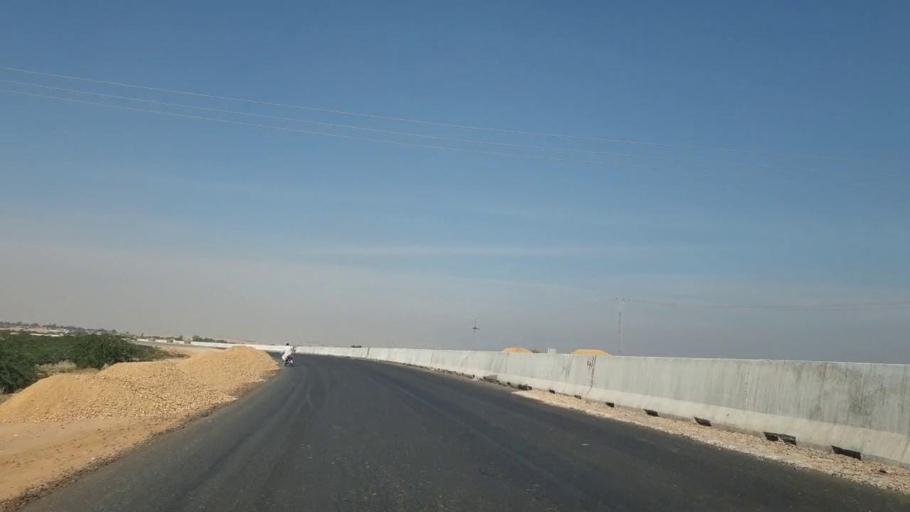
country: PK
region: Sindh
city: Matiari
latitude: 25.6547
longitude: 68.3007
